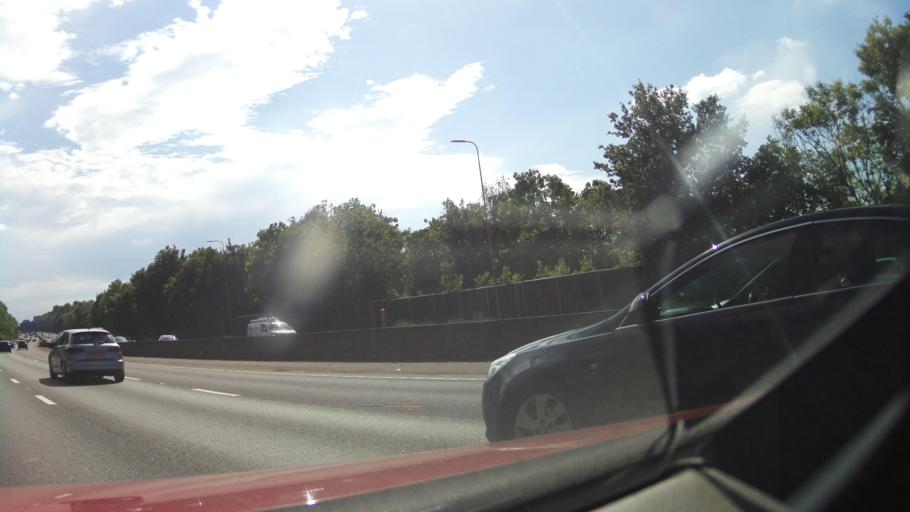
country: GB
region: England
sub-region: Manchester
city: Swinton
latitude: 53.5098
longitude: -2.3716
